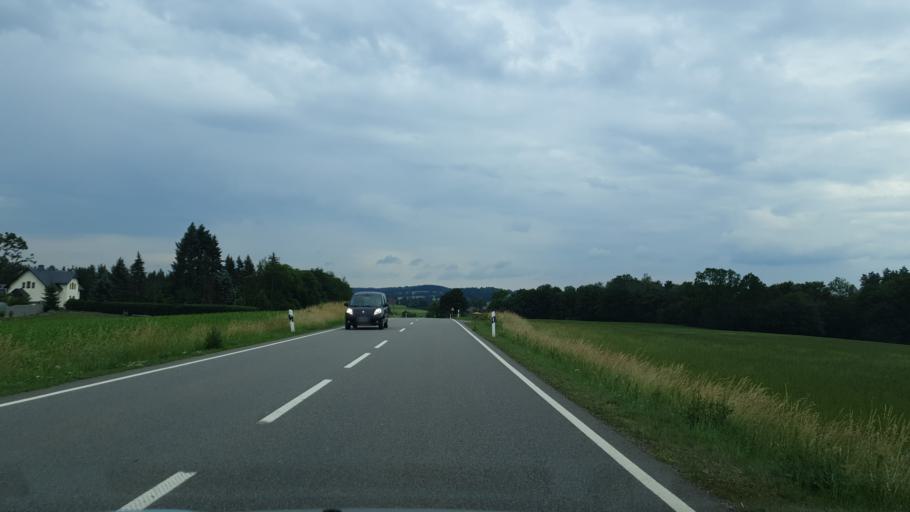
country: DE
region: Saxony
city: Hirschfeld
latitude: 50.6214
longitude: 12.4319
